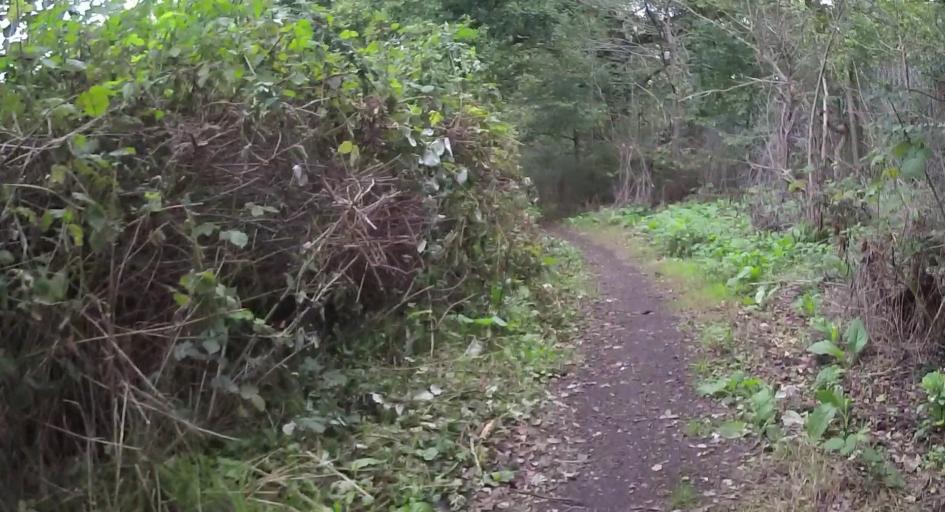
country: GB
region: England
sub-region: Surrey
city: Byfleet
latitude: 51.3279
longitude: -0.4806
